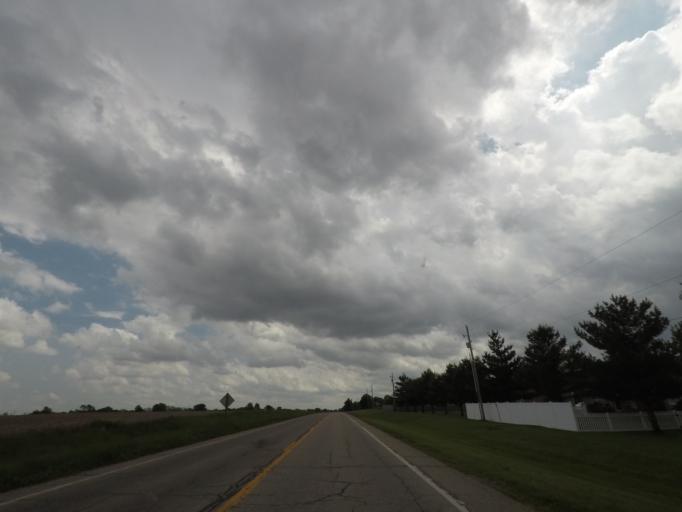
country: US
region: Illinois
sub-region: De Witt County
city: Clinton
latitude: 40.1709
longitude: -88.9605
